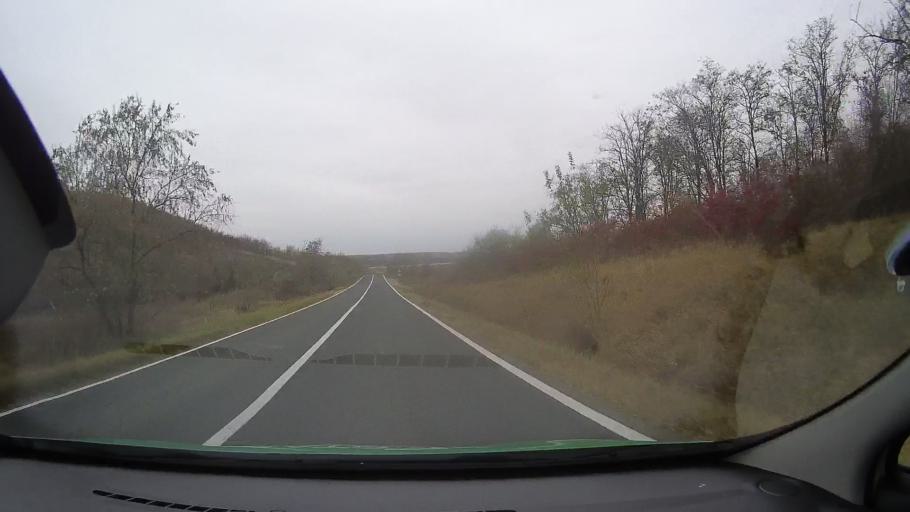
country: RO
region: Constanta
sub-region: Comuna Garliciu
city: Garliciu
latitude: 44.7067
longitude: 28.0688
